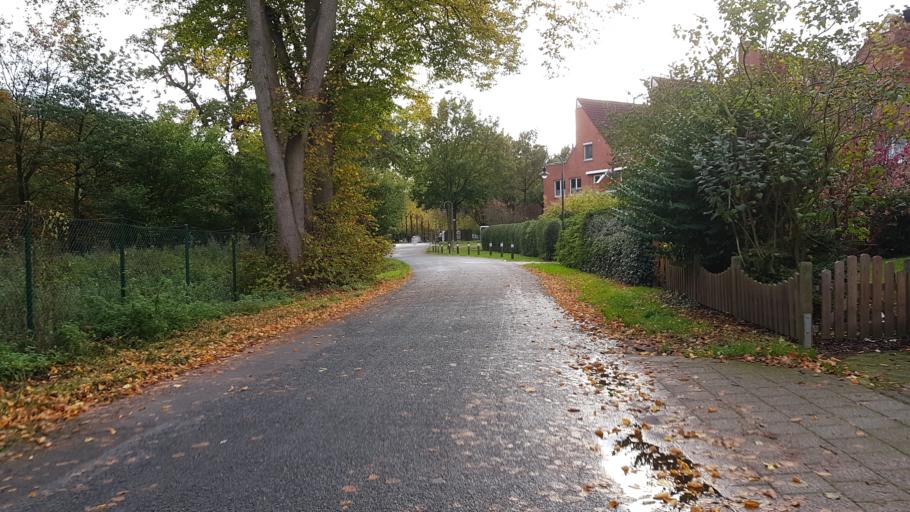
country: DE
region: Bremen
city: Bremen
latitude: 53.0964
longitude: 8.8226
